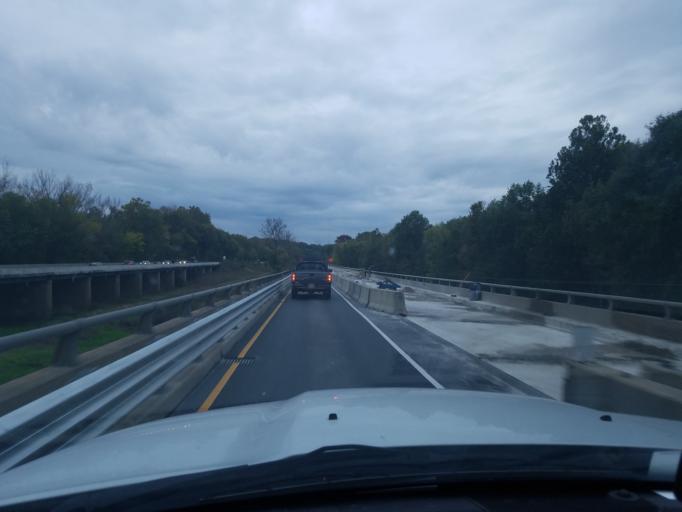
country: US
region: Kentucky
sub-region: Henderson County
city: Henderson
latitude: 37.8993
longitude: -87.5532
